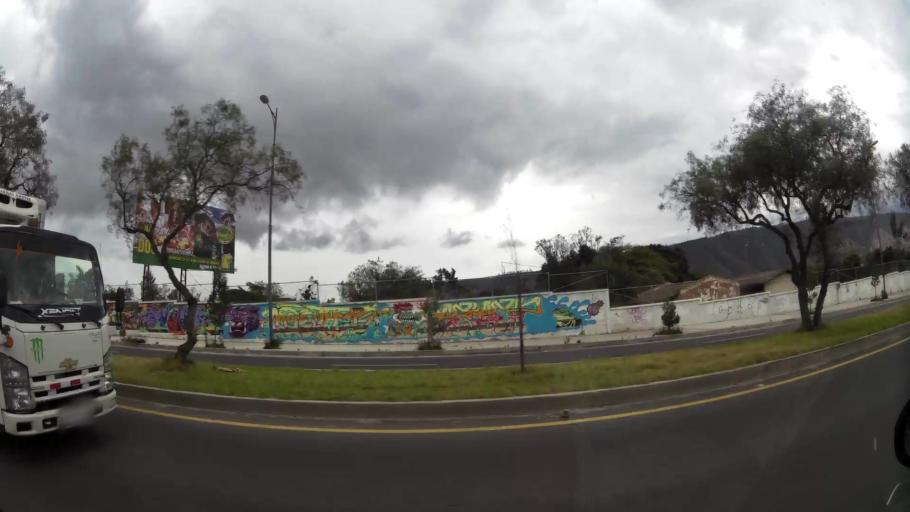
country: EC
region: Pichincha
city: Quito
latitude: -0.0108
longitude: -78.4531
